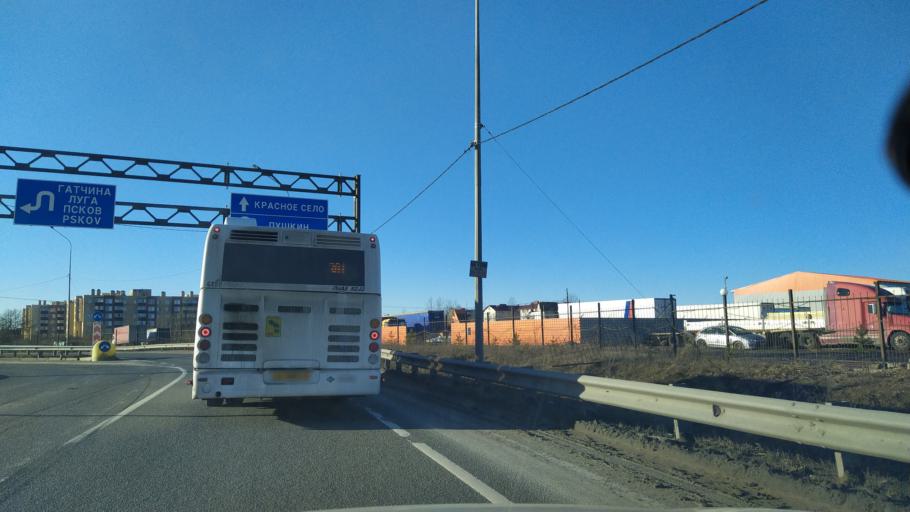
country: RU
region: St.-Petersburg
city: Aleksandrovskaya
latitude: 59.7206
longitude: 30.2740
